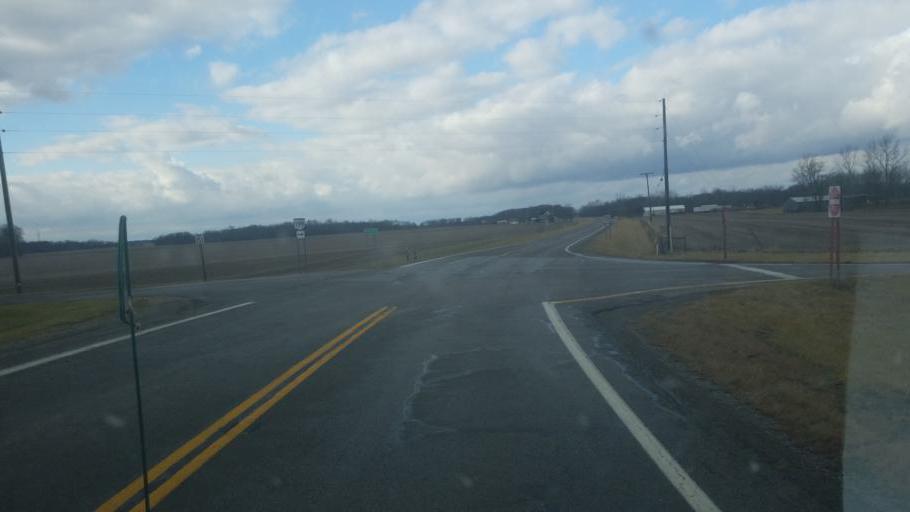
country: US
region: Ohio
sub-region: Wyandot County
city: Upper Sandusky
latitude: 40.7821
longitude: -83.2467
